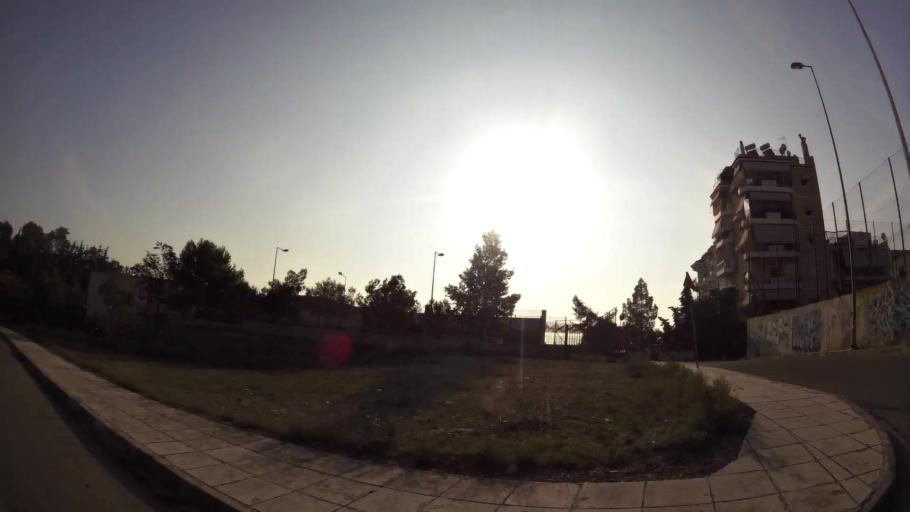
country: GR
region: Attica
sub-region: Nomos Piraios
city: Nikaia
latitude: 37.9719
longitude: 23.6359
